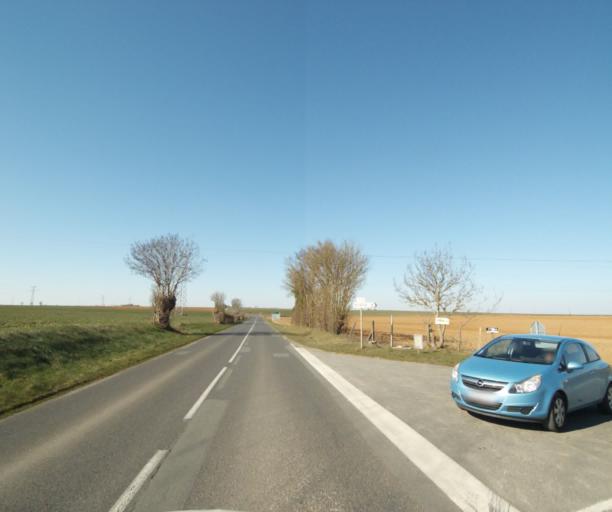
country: FR
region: Poitou-Charentes
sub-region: Departement des Deux-Sevres
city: Saint-Maxire
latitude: 46.3605
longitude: -0.4857
